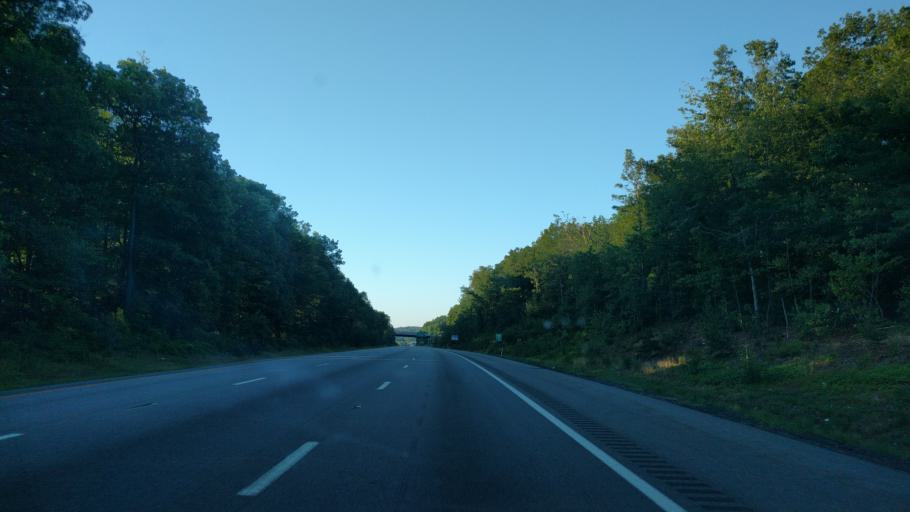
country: US
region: Massachusetts
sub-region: Middlesex County
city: Marlborough
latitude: 42.3281
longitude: -71.5747
